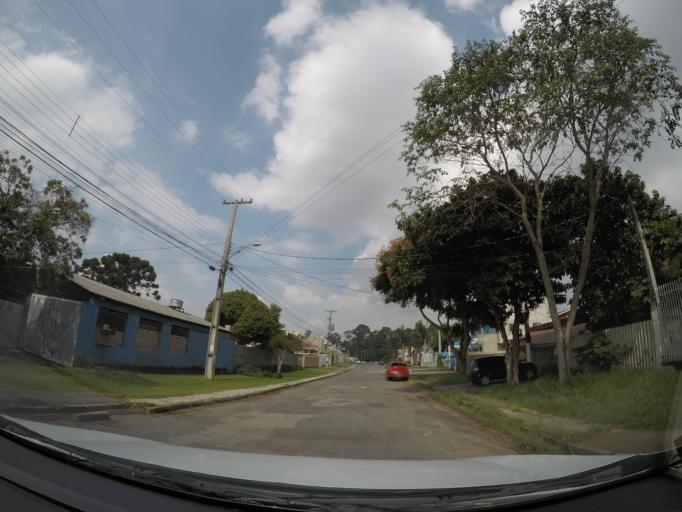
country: BR
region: Parana
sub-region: Sao Jose Dos Pinhais
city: Sao Jose dos Pinhais
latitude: -25.5026
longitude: -49.2410
